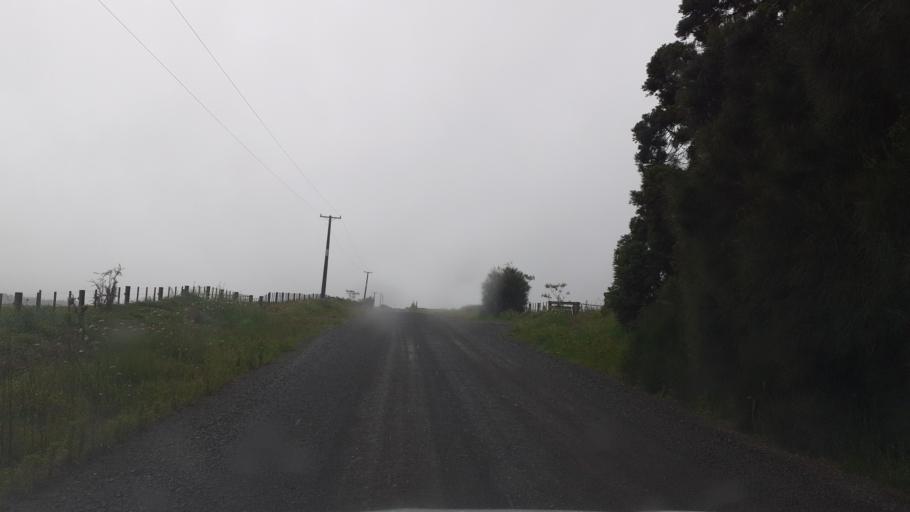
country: NZ
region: Northland
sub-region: Far North District
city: Kerikeri
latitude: -35.2244
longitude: 173.8745
